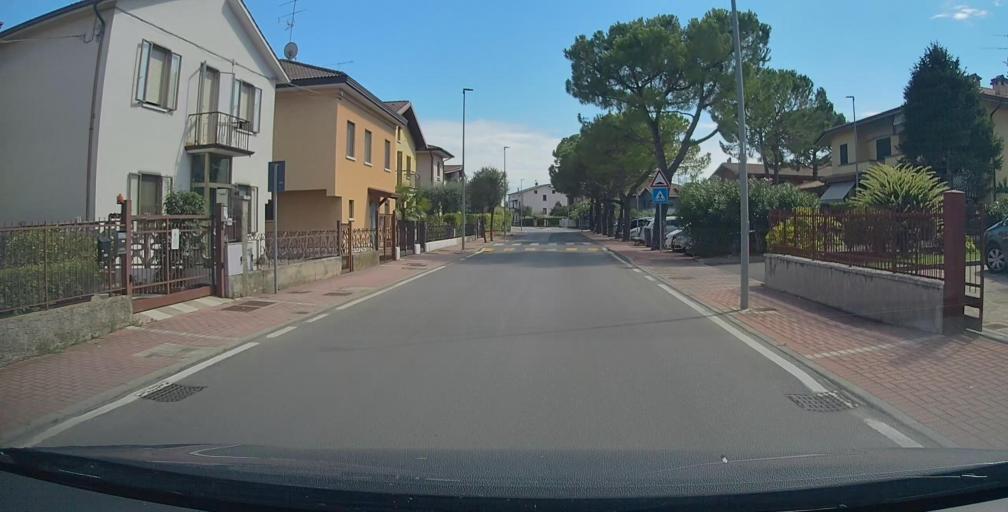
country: IT
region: Lombardy
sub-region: Provincia di Brescia
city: San Martino della Battaglia
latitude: 45.4576
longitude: 10.6144
